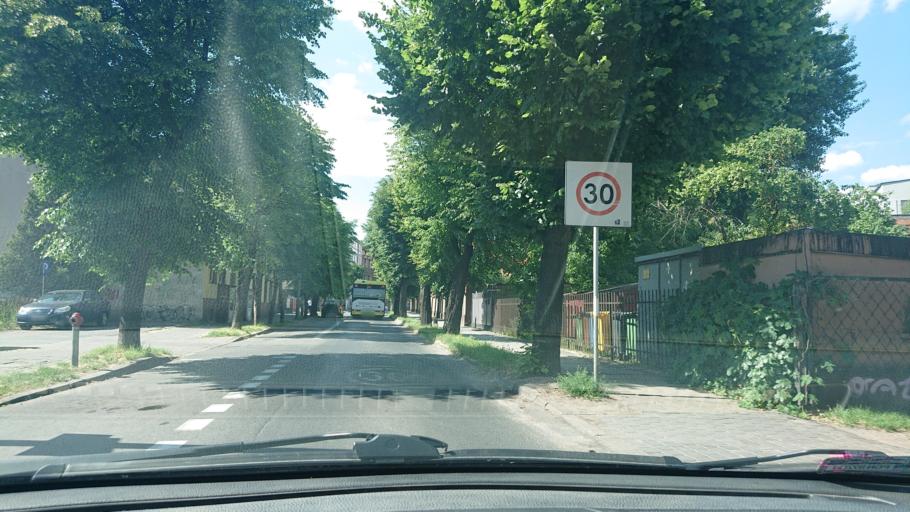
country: PL
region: Greater Poland Voivodeship
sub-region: Powiat gnieznienski
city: Gniezno
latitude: 52.5312
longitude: 17.5950
